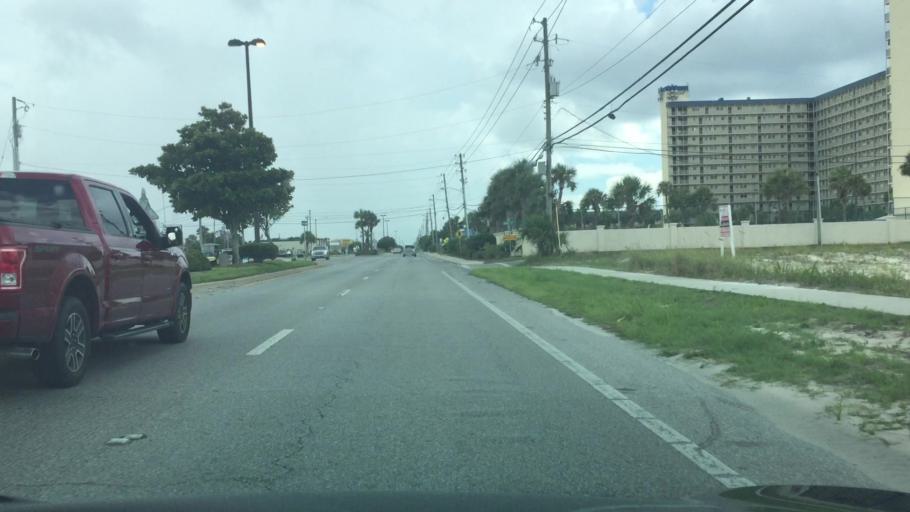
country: US
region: Florida
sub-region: Bay County
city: Lower Grand Lagoon
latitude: 30.1485
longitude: -85.7621
